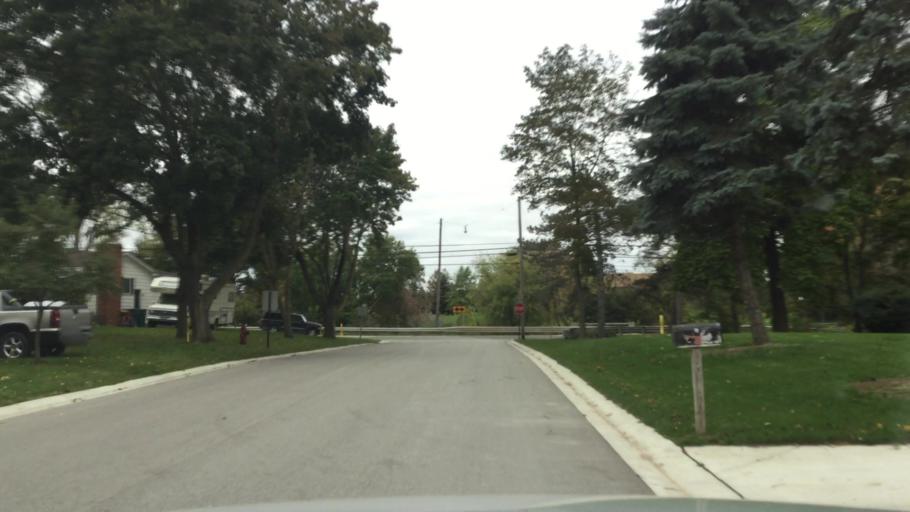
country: US
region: Michigan
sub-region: Macomb County
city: Richmond
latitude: 42.8211
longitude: -82.7599
